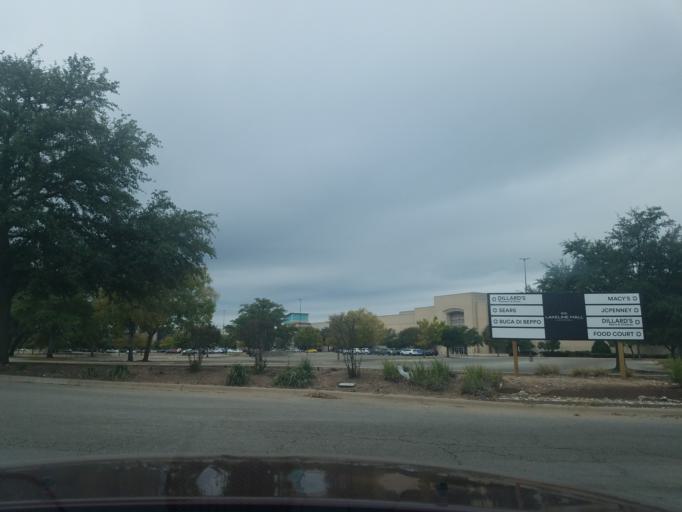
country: US
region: Texas
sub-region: Williamson County
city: Anderson Mill
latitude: 30.4711
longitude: -97.8038
